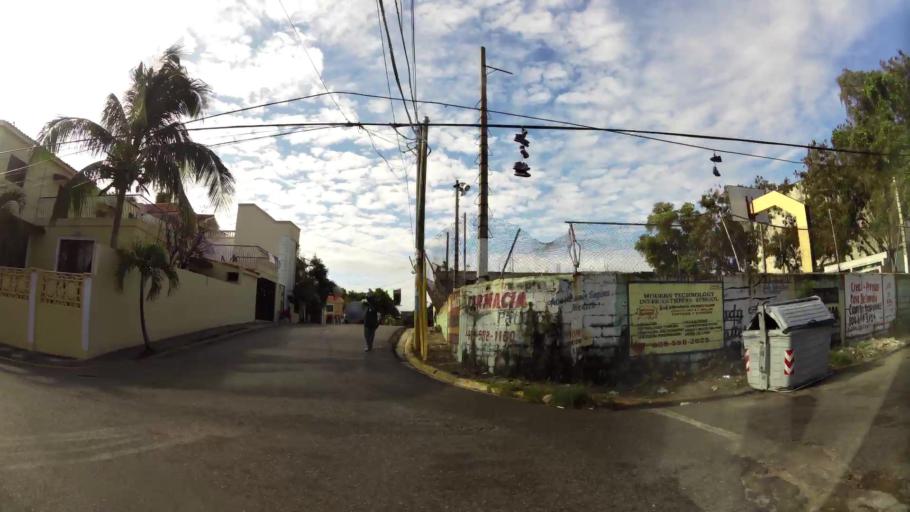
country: DO
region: Santo Domingo
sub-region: Santo Domingo
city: Santo Domingo Este
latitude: 18.4868
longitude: -69.8617
